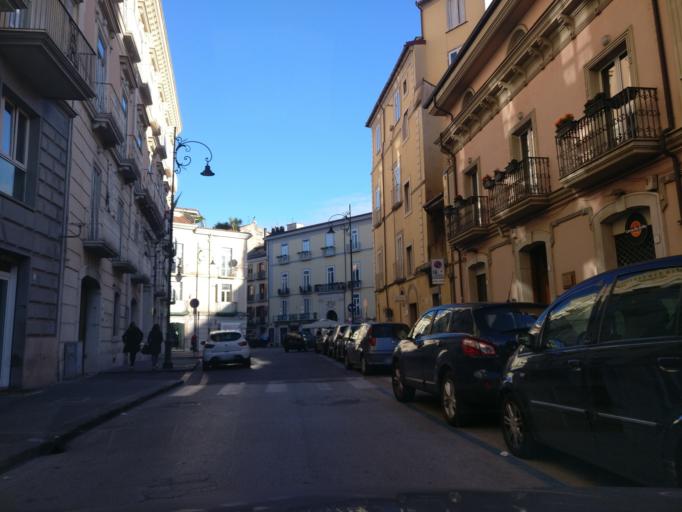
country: IT
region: Campania
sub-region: Provincia di Avellino
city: Avellino
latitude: 40.9146
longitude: 14.7901
